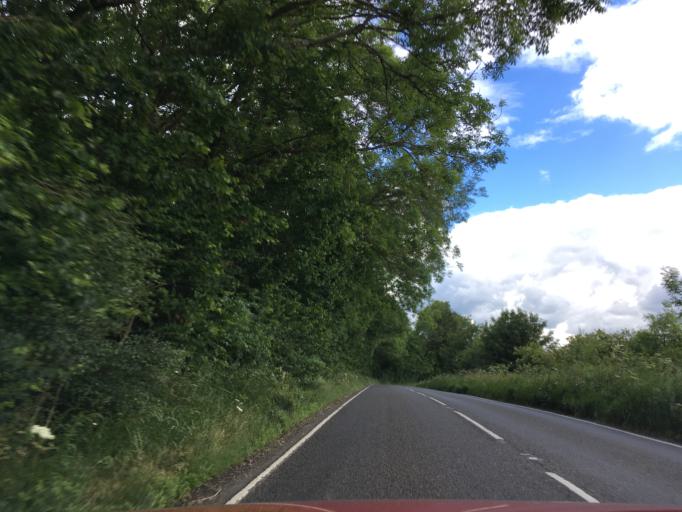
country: GB
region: England
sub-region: Oxfordshire
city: Chipping Norton
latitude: 51.8953
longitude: -1.5626
